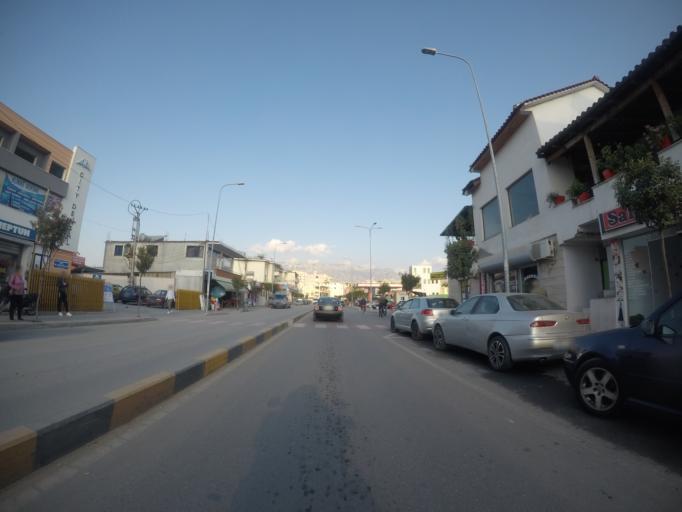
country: AL
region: Durres
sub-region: Rrethi i Krujes
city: Fushe-Kruje
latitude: 41.4788
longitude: 19.7170
